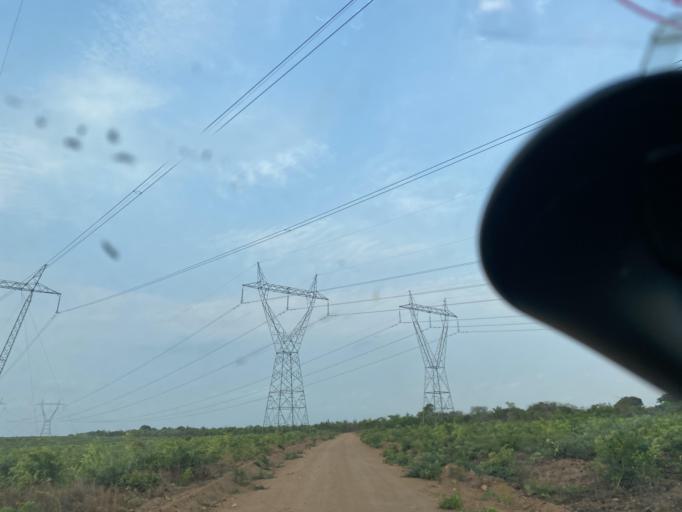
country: ZM
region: Lusaka
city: Chongwe
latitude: -15.2038
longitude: 28.5194
